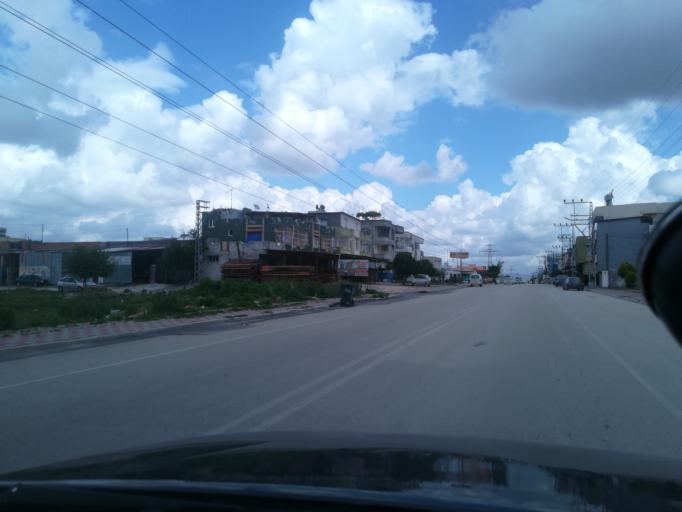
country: TR
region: Adana
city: Yuregir
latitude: 36.9755
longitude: 35.3916
